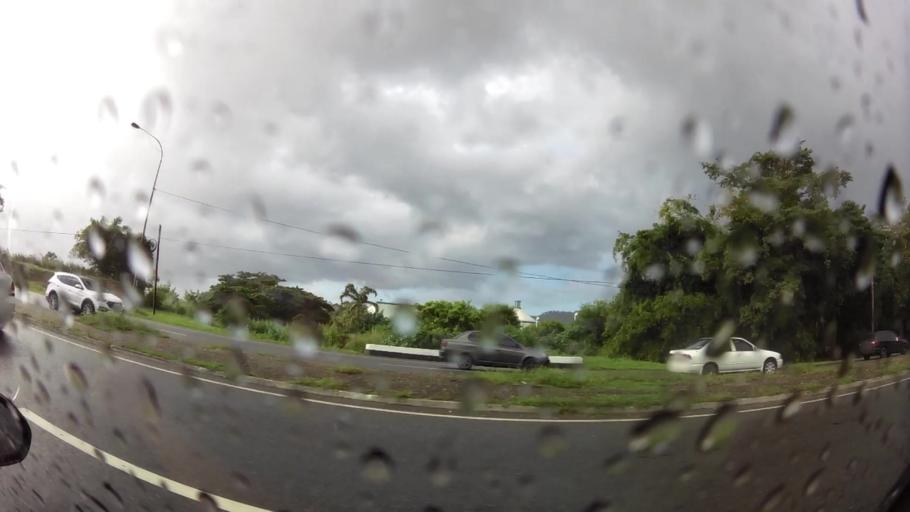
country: TT
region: Tunapuna/Piarco
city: Tunapuna
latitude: 10.6429
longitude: -61.4302
